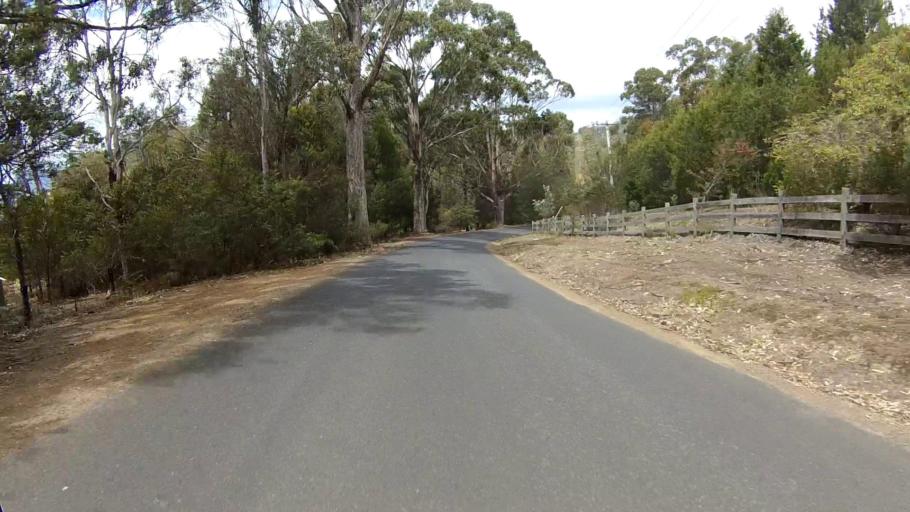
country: AU
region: Tasmania
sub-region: Sorell
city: Sorell
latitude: -42.5909
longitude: 147.9154
